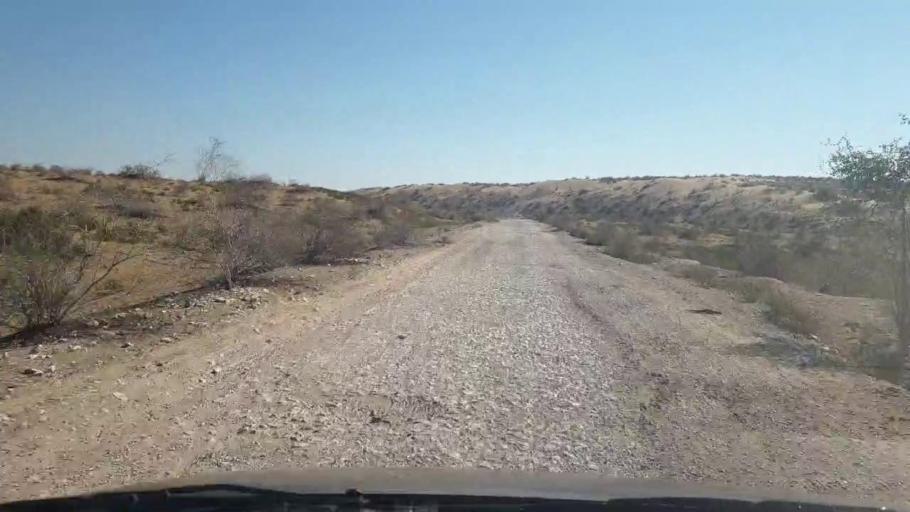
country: PK
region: Sindh
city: Bozdar
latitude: 27.0145
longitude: 68.7376
